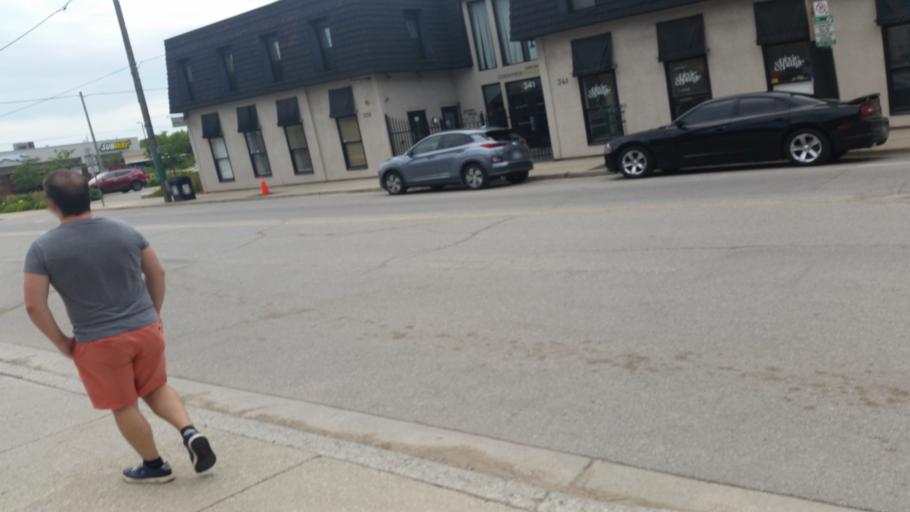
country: CA
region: Ontario
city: London
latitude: 42.9813
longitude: -81.2509
